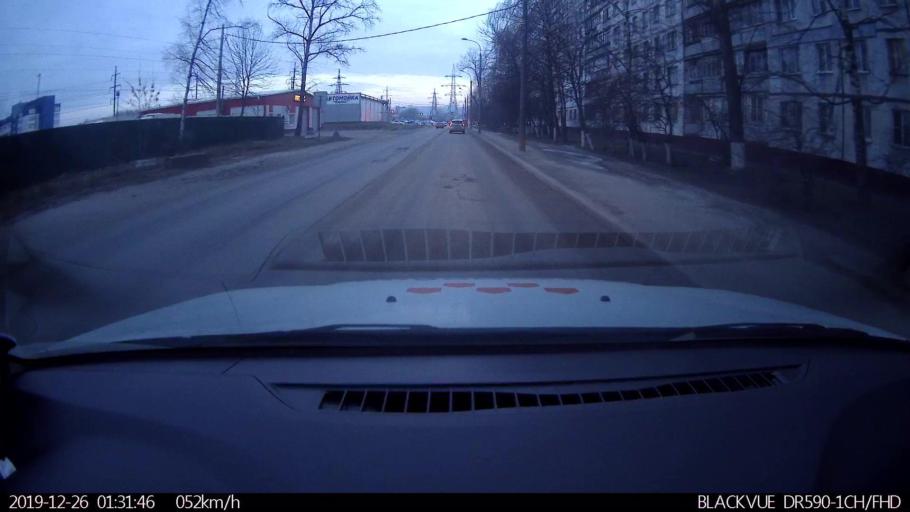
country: RU
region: Nizjnij Novgorod
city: Nizhniy Novgorod
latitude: 56.2653
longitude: 43.9015
